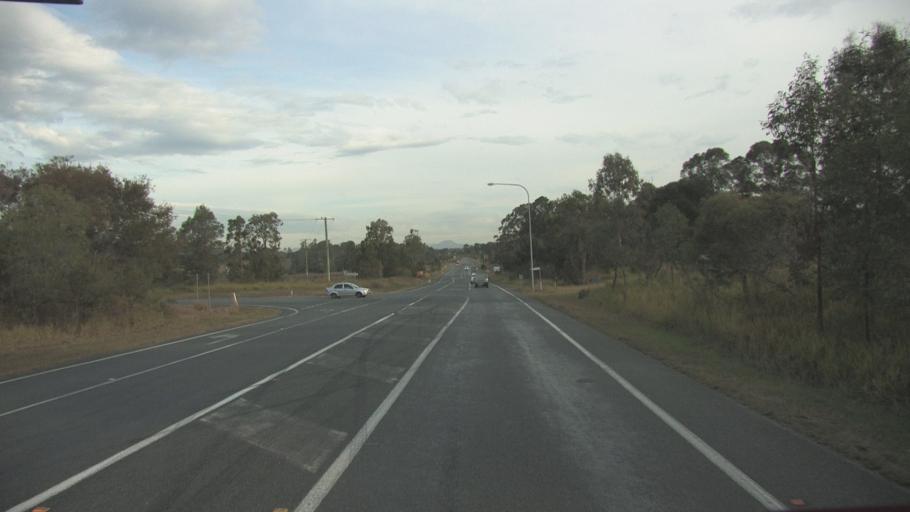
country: AU
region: Queensland
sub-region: Logan
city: Cedar Vale
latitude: -27.8532
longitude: 153.1212
